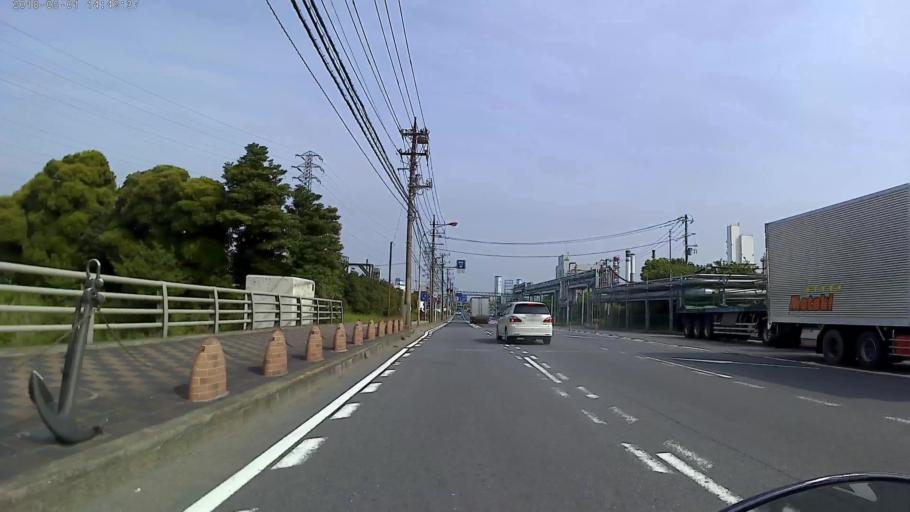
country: JP
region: Kanagawa
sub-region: Kawasaki-shi
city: Kawasaki
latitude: 35.5236
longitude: 139.7522
